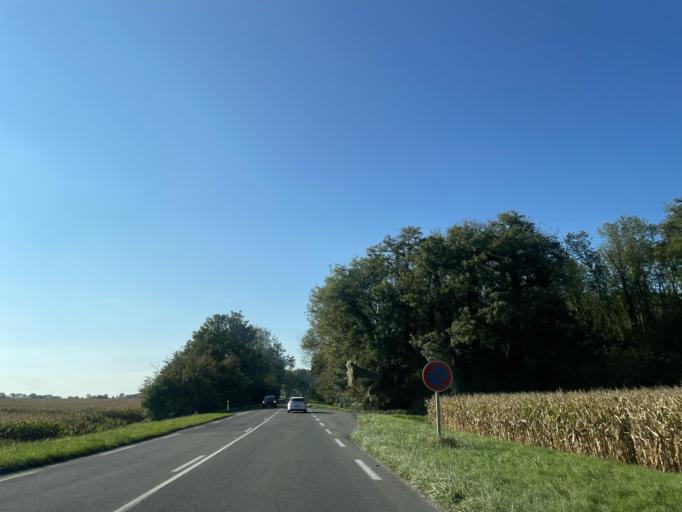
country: FR
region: Ile-de-France
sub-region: Departement de Seine-et-Marne
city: Guerard
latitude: 48.8374
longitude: 2.9790
